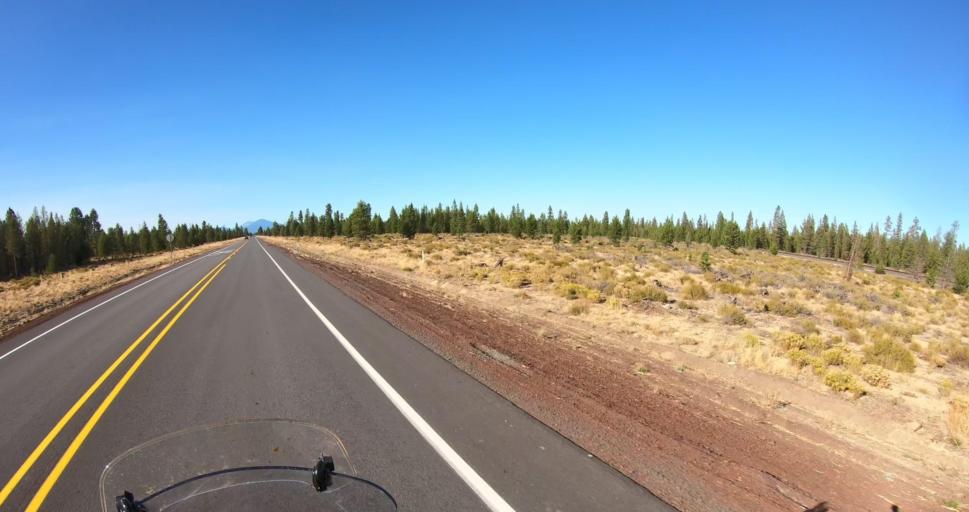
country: US
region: Oregon
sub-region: Deschutes County
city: La Pine
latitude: 43.6085
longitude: -121.5020
